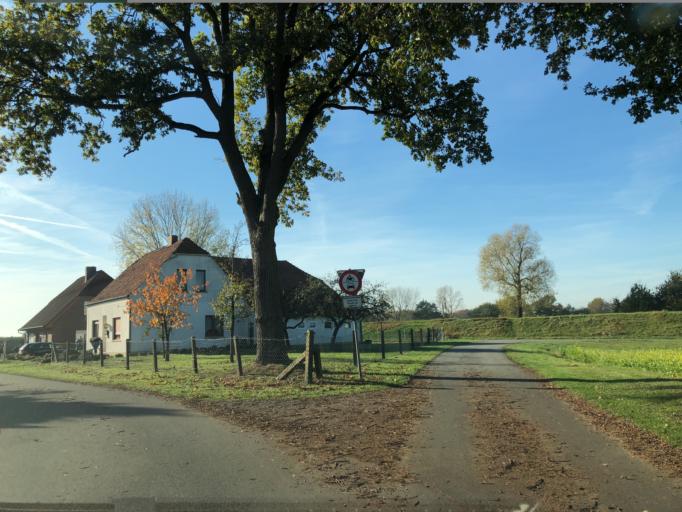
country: DE
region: Lower Saxony
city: Lehe
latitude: 53.0251
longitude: 7.3216
